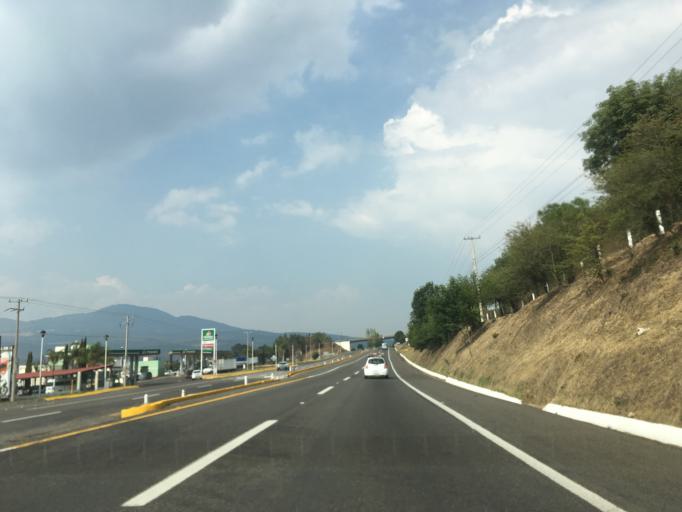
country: MX
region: Michoacan
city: Lagunillas
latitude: 19.5560
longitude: -101.4241
